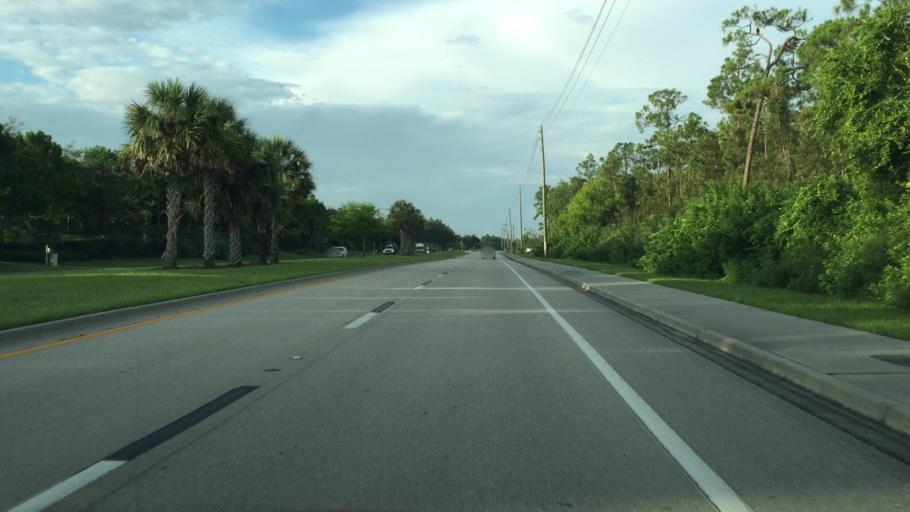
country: US
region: Florida
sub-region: Lee County
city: Gateway
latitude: 26.5597
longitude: -81.7867
